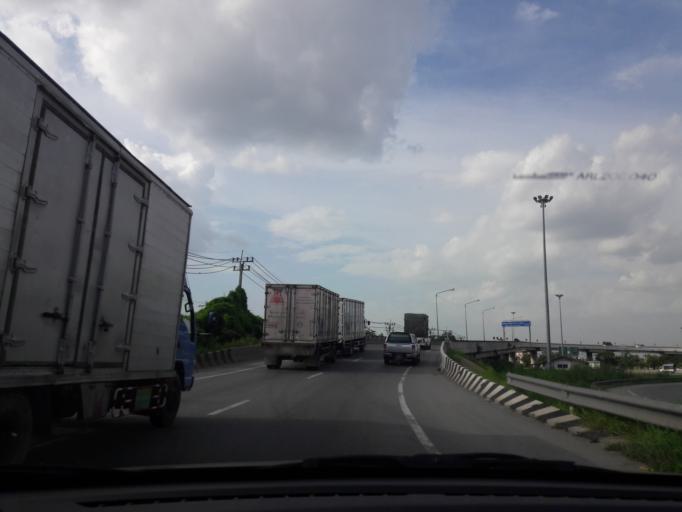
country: TH
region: Bangkok
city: Bang Bon
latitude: 13.6430
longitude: 100.4082
